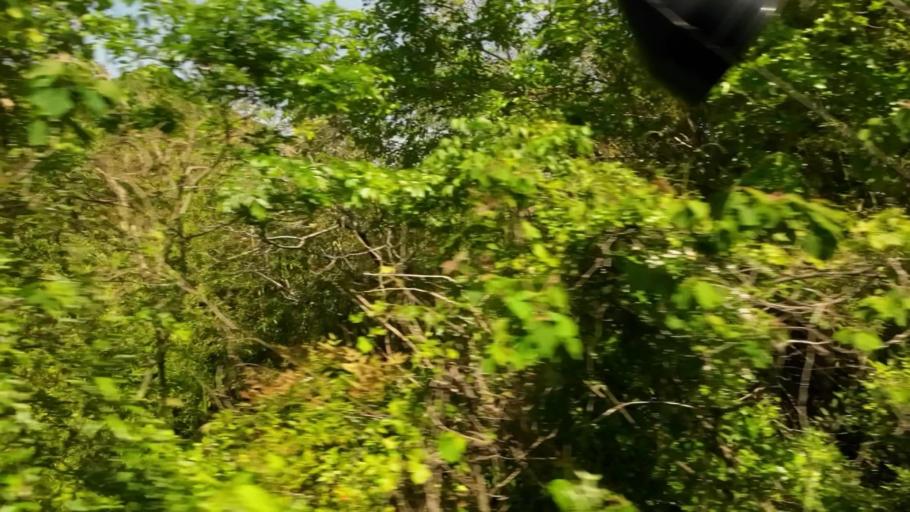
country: JP
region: Tokushima
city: Ikedacho
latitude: 33.9955
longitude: 133.7935
